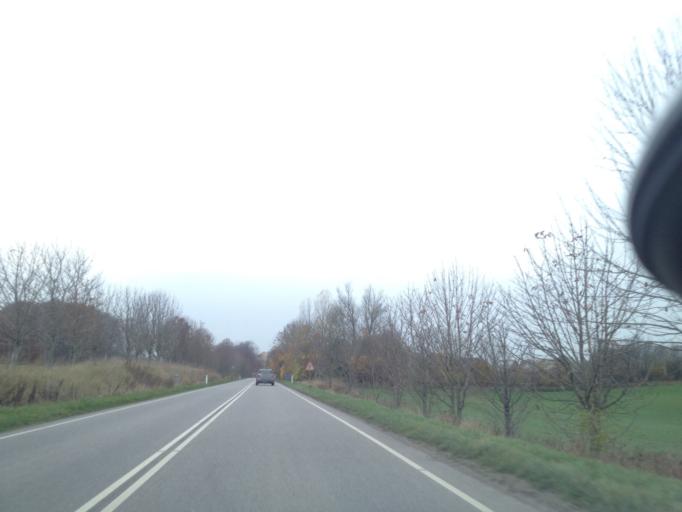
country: DK
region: South Denmark
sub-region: Assens Kommune
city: Vissenbjerg
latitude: 55.4585
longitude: 10.1106
